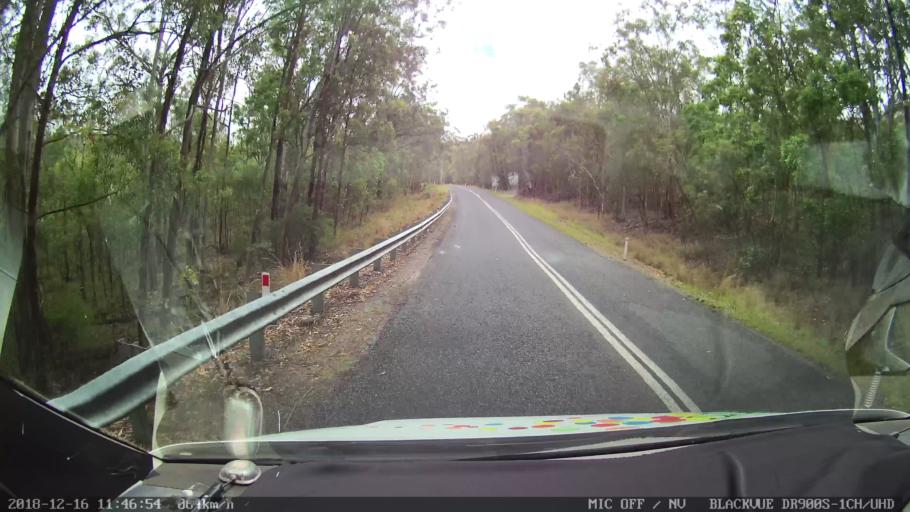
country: AU
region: New South Wales
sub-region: Tenterfield Municipality
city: Carrolls Creek
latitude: -28.9249
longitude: 152.2332
